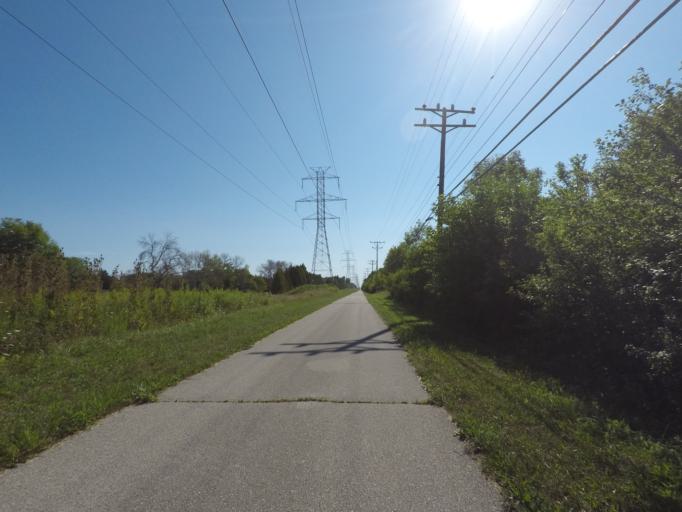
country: US
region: Wisconsin
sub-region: Waukesha County
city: New Berlin
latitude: 43.0110
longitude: -88.1016
